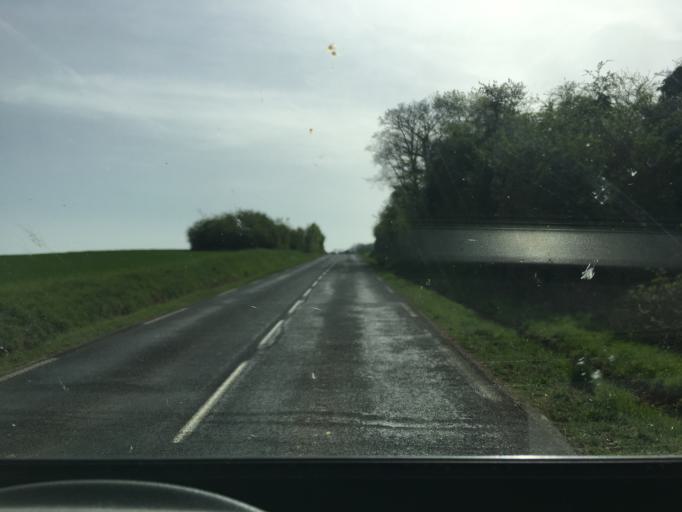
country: FR
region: Lorraine
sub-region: Departement de Meurthe-et-Moselle
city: Gondreville
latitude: 48.6627
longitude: 5.9632
